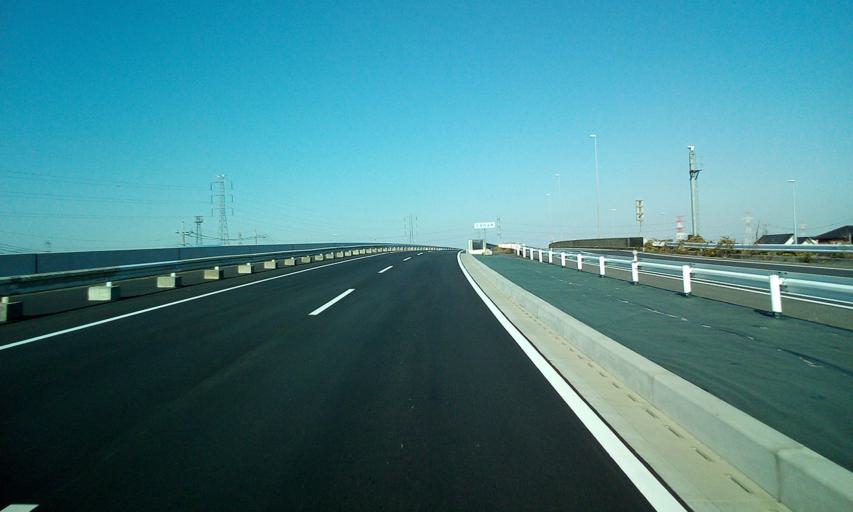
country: JP
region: Saitama
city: Satte
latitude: 36.1102
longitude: 139.7478
